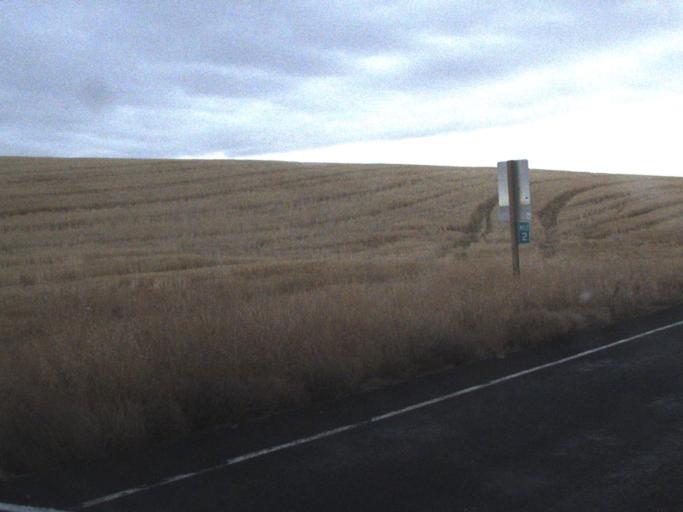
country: US
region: Washington
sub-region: Lincoln County
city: Davenport
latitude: 47.6838
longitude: -118.1410
